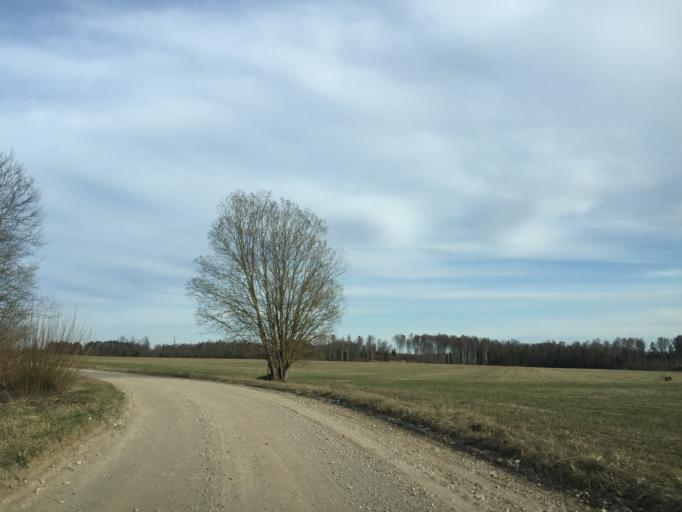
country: LV
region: Kegums
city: Kegums
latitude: 56.7958
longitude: 24.7559
